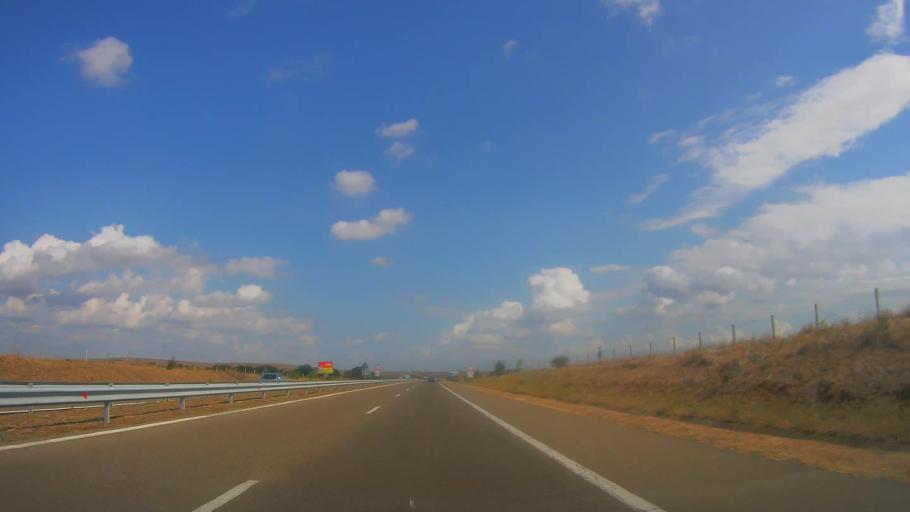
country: BG
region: Burgas
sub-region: Obshtina Karnobat
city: Karnobat
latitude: 42.5897
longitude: 27.0701
